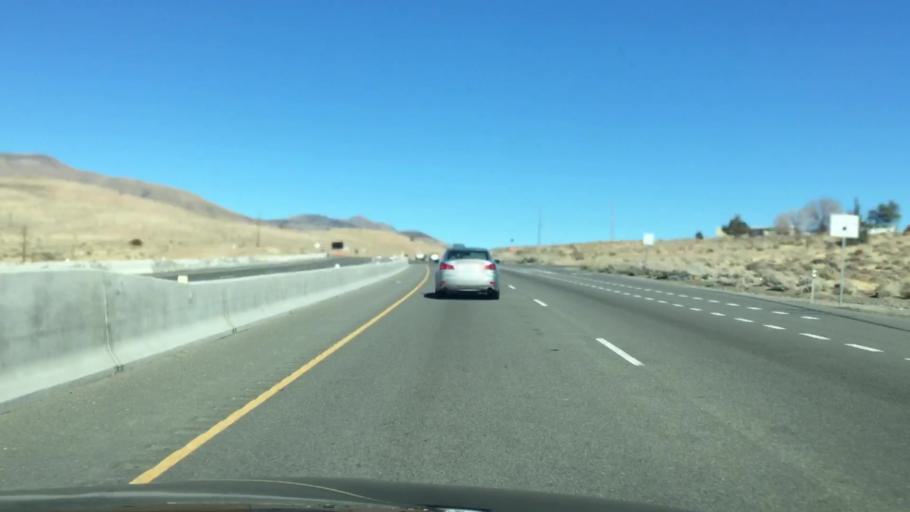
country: US
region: Nevada
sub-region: Carson City
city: Carson City
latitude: 39.1998
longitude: -119.6883
